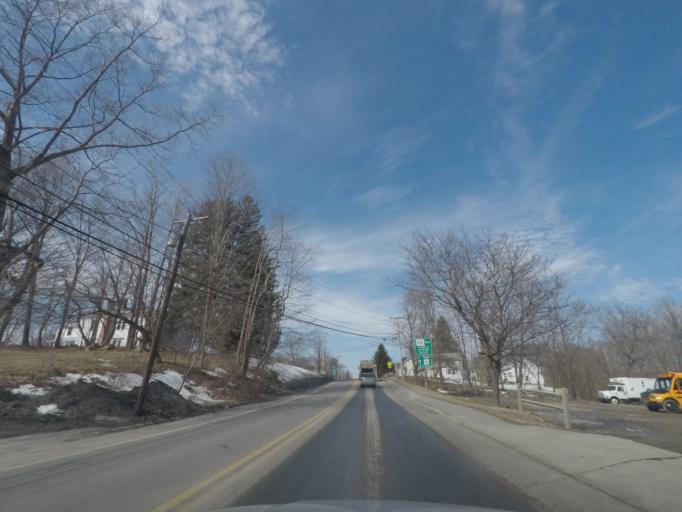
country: US
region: Massachusetts
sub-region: Berkshire County
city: West Stockbridge
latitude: 42.3362
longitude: -73.3696
